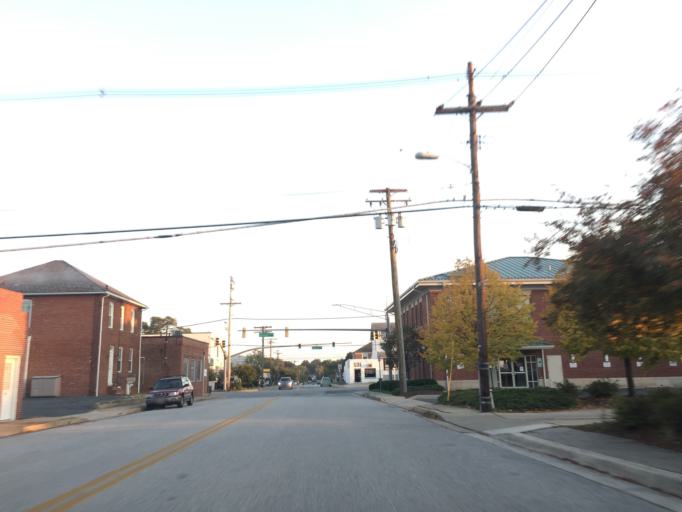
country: US
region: Maryland
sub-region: Baltimore County
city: Essex
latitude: 39.3099
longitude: -76.4741
